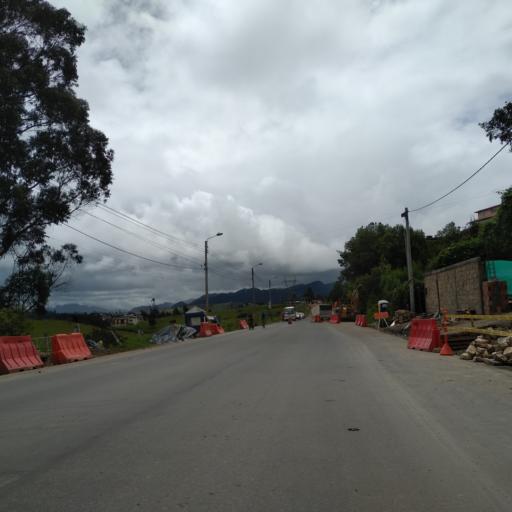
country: CO
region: Cundinamarca
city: La Calera
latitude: 4.7021
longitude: -73.9805
